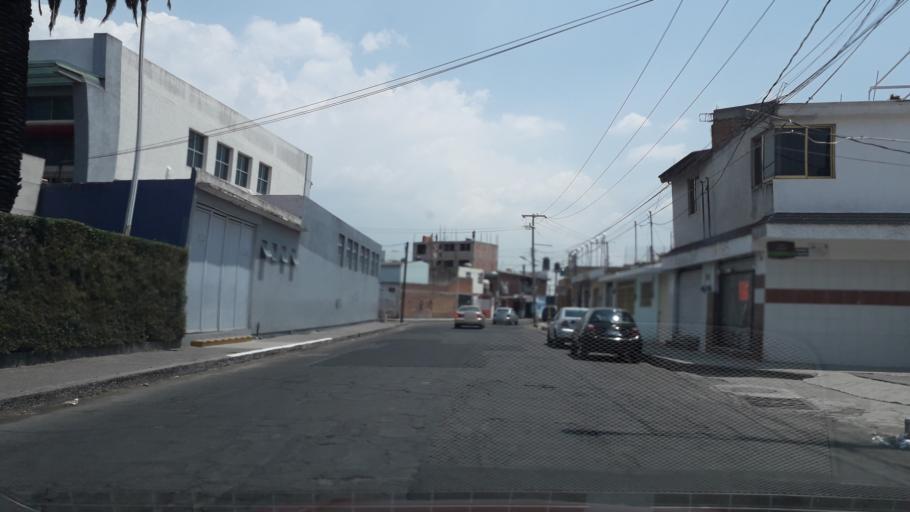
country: MX
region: Puebla
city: Puebla
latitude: 19.0467
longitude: -98.1710
